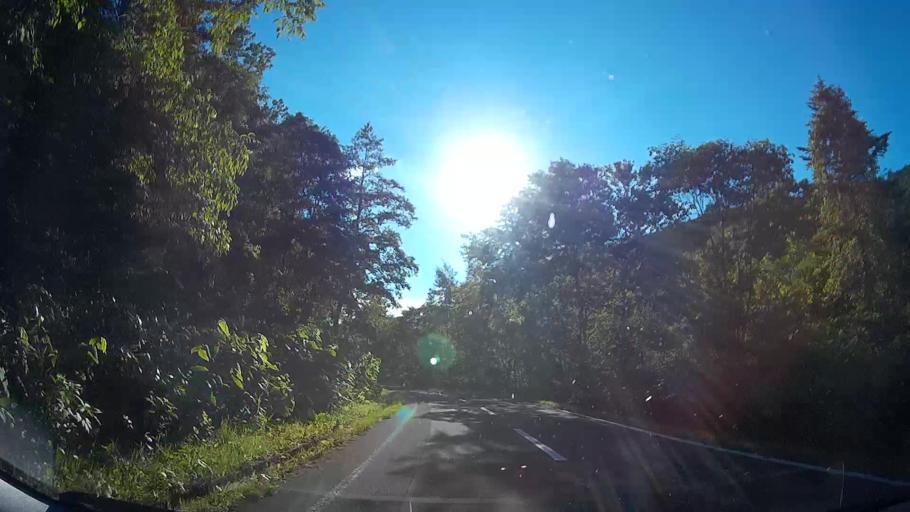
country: JP
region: Hokkaido
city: Otaru
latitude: 42.9952
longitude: 141.0948
